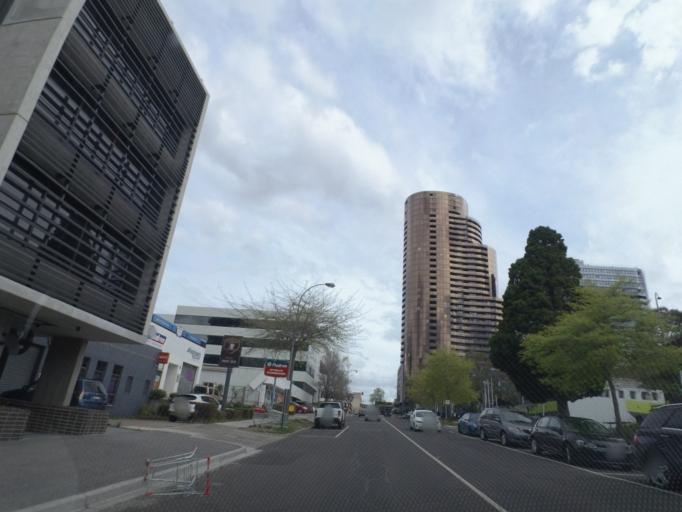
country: AU
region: Victoria
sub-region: Whitehorse
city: Box Hill
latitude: -37.8161
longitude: 145.1196
